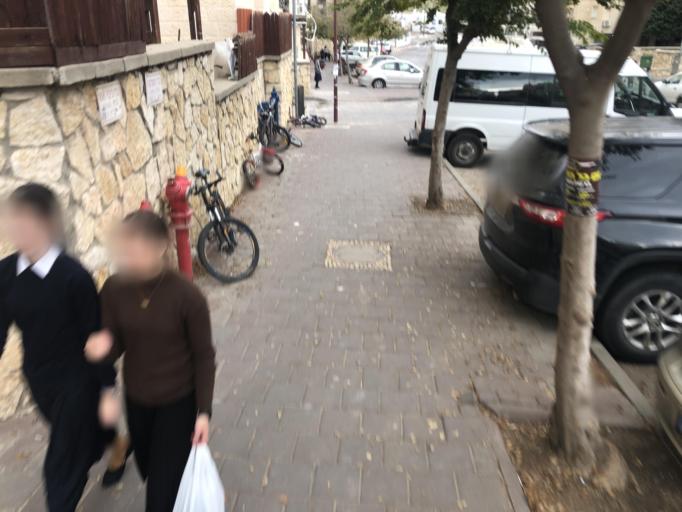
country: IL
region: Jerusalem
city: Modiin Ilit
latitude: 31.9380
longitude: 35.0462
